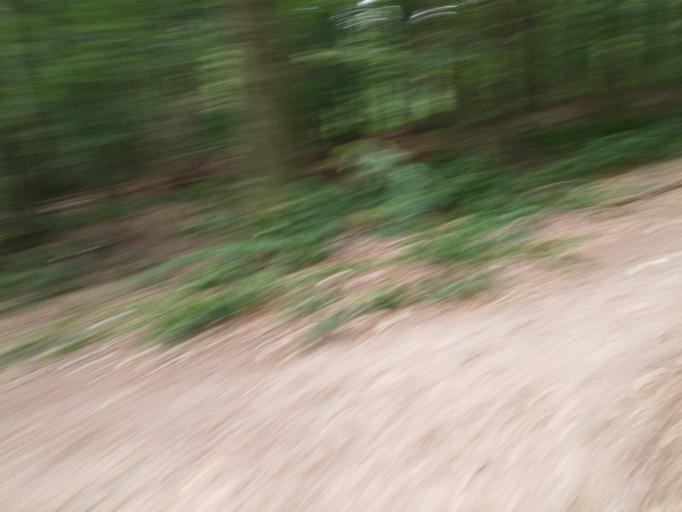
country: DE
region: Bavaria
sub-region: Regierungsbezirk Mittelfranken
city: Seukendorf
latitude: 49.4865
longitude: 10.9094
